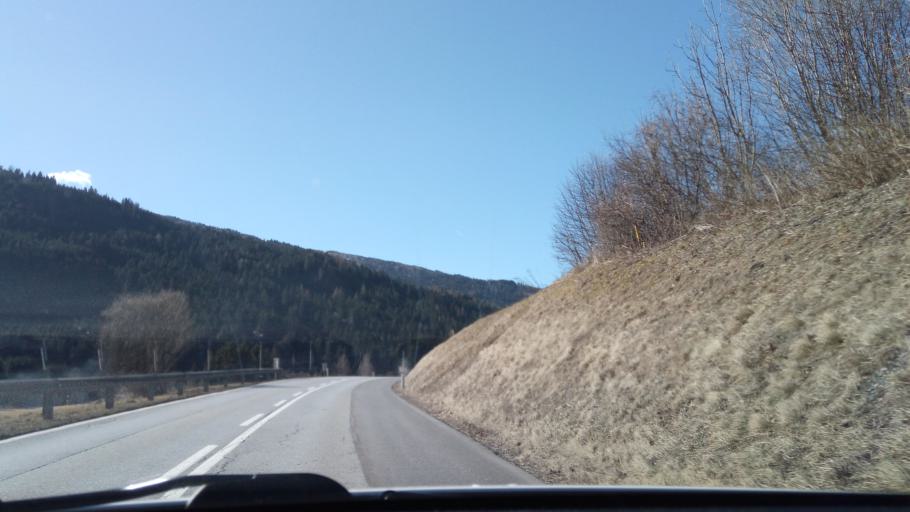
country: AT
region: Styria
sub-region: Politischer Bezirk Murau
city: Murau
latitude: 47.1103
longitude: 14.1412
